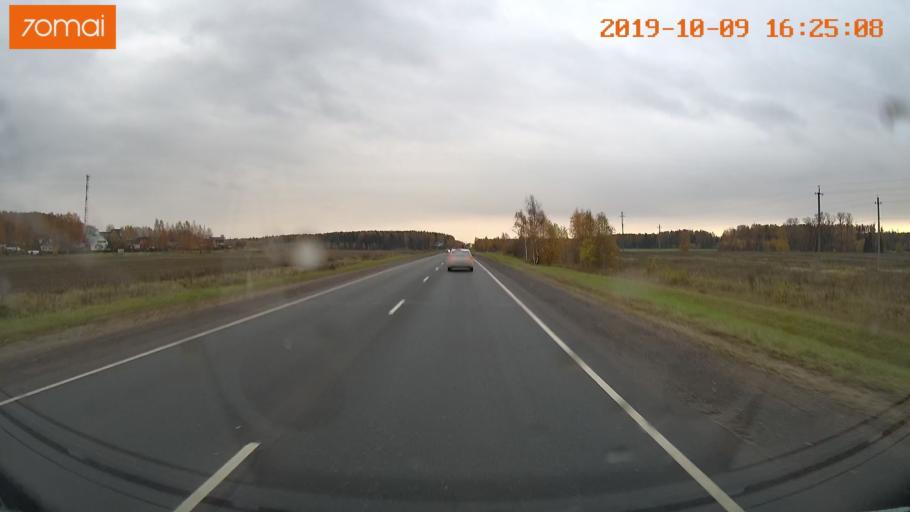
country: RU
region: Kostroma
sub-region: Kostromskoy Rayon
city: Kostroma
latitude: 57.6451
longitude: 40.9172
